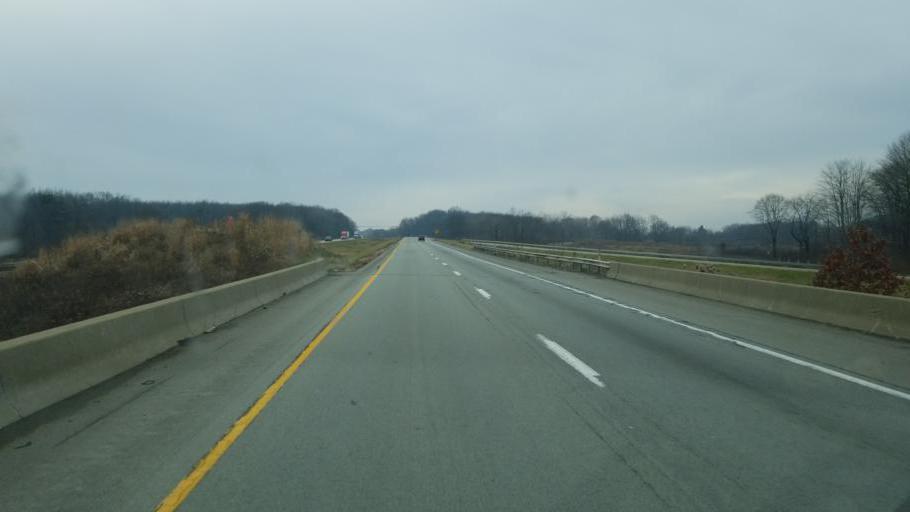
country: US
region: Pennsylvania
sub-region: Mercer County
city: Mercer
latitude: 41.1930
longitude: -80.2408
